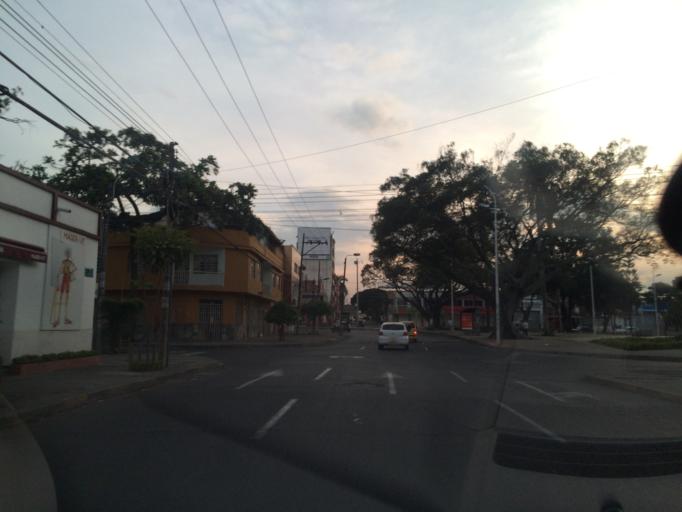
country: CO
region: Valle del Cauca
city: Cali
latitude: 3.4367
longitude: -76.5372
